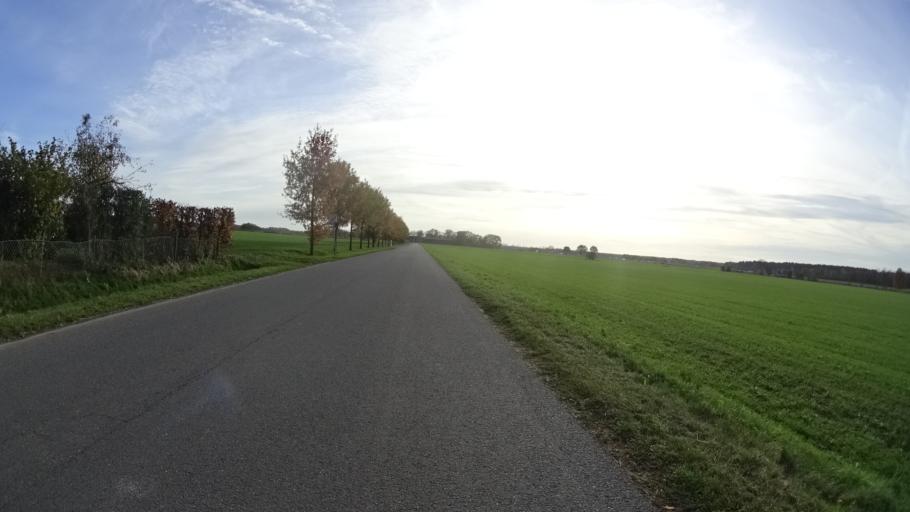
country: DE
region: Lower Saxony
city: Wendisch Evern
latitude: 53.2304
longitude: 10.4589
